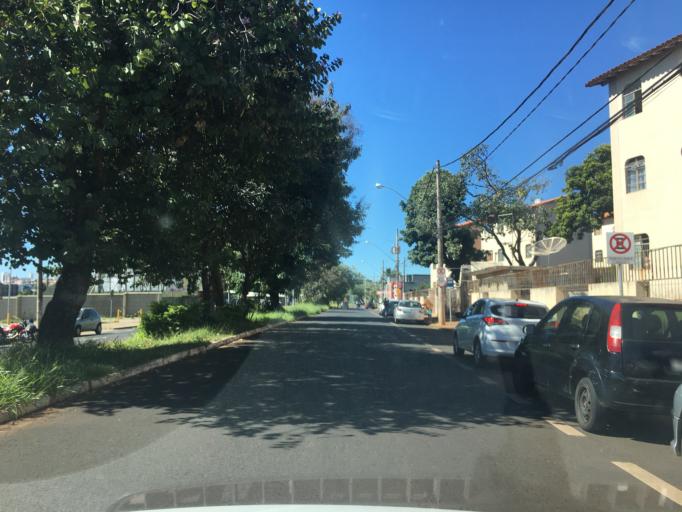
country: BR
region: Minas Gerais
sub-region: Uberlandia
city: Uberlandia
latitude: -18.9332
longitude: -48.2844
